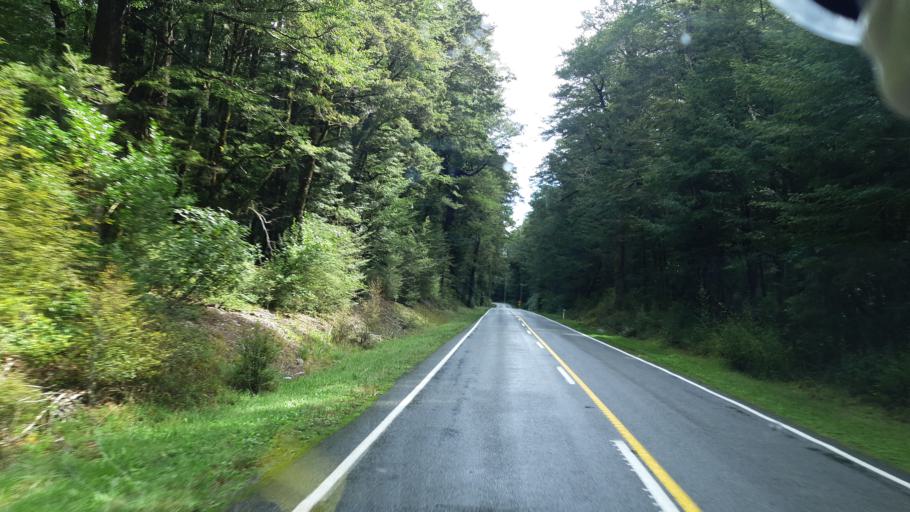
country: NZ
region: Canterbury
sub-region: Hurunui District
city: Amberley
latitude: -42.3807
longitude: 172.3102
